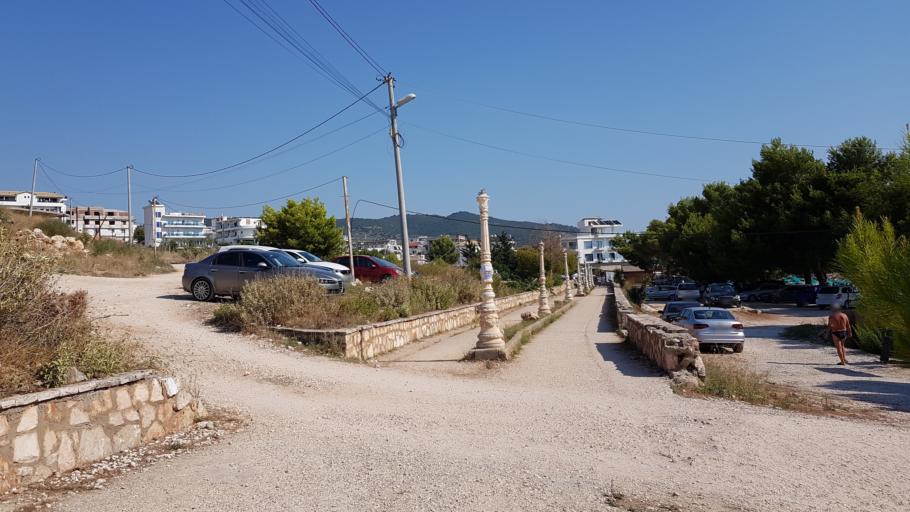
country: AL
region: Vlore
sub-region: Rrethi i Sarandes
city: Xarre
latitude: 39.7745
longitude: 20.0021
